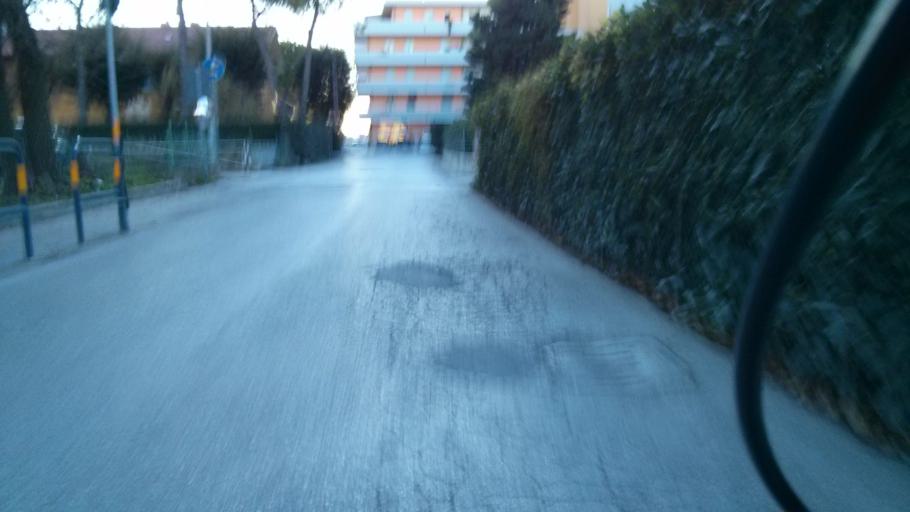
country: IT
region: The Marches
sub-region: Provincia di Pesaro e Urbino
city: Fano
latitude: 43.8345
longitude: 13.0275
